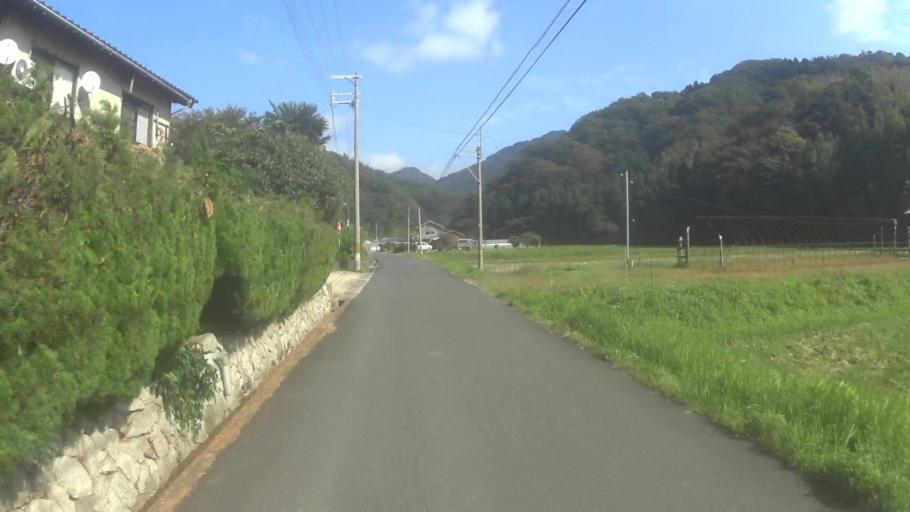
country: JP
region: Kyoto
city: Miyazu
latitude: 35.7160
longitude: 135.1188
